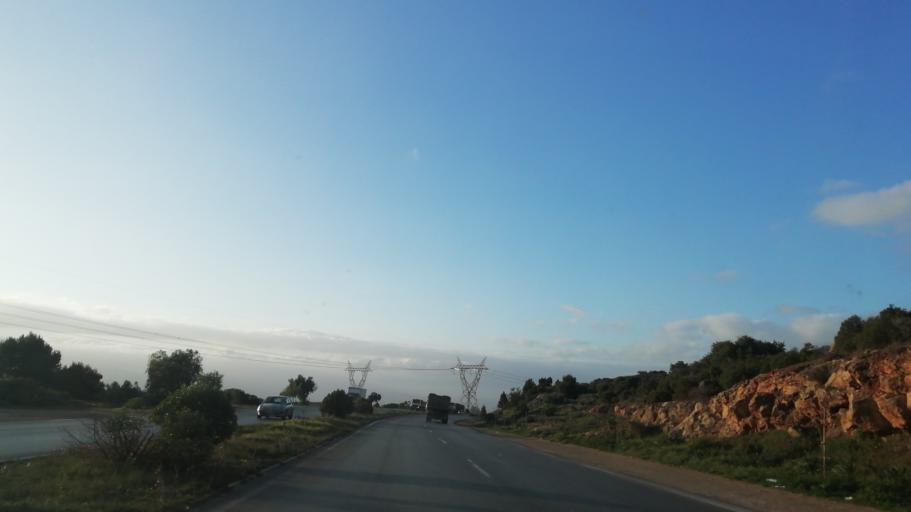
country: DZ
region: Oran
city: Es Senia
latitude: 35.6357
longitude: -0.7110
